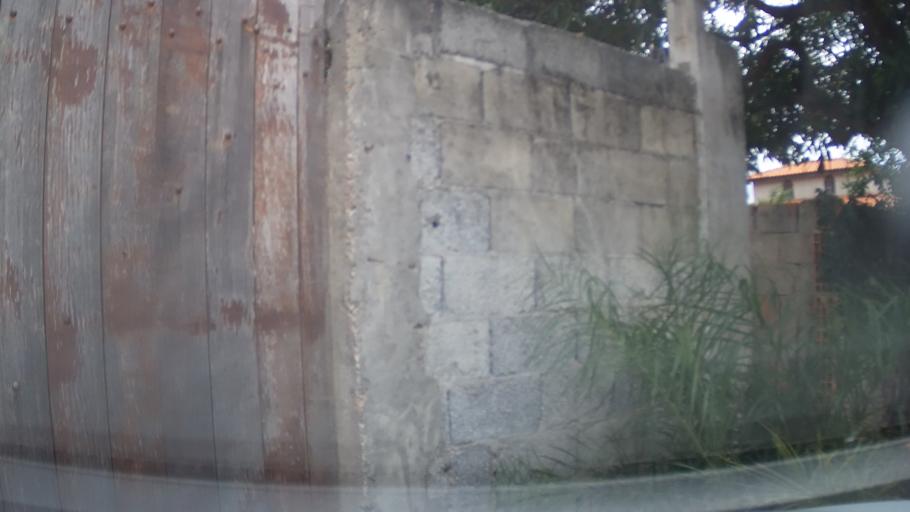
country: BR
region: Sao Paulo
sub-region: Itupeva
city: Itupeva
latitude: -23.1679
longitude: -47.0073
